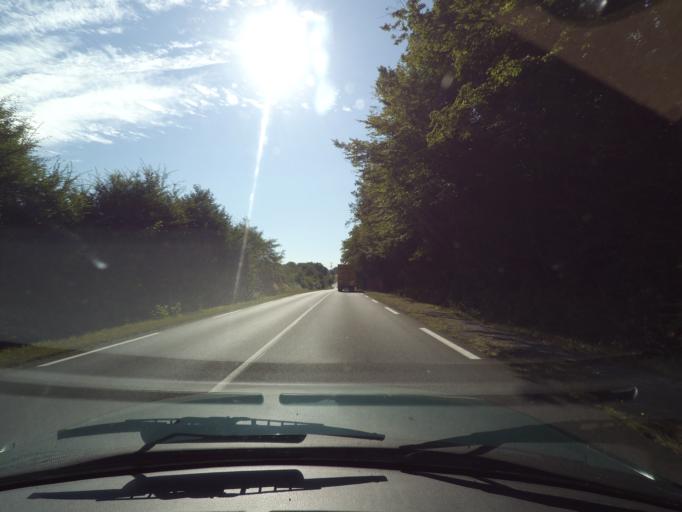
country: FR
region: Poitou-Charentes
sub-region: Departement de la Vienne
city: Lussac-les-Chateaux
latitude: 46.4250
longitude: 0.6265
